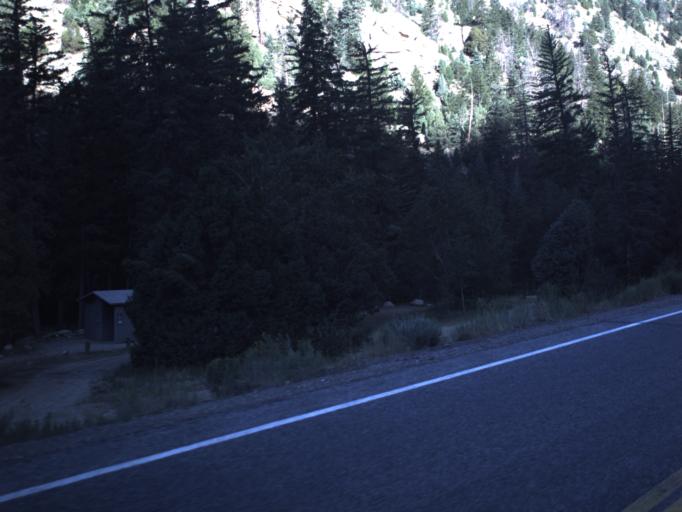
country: US
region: Utah
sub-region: Emery County
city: Huntington
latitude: 39.4468
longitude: -111.1379
